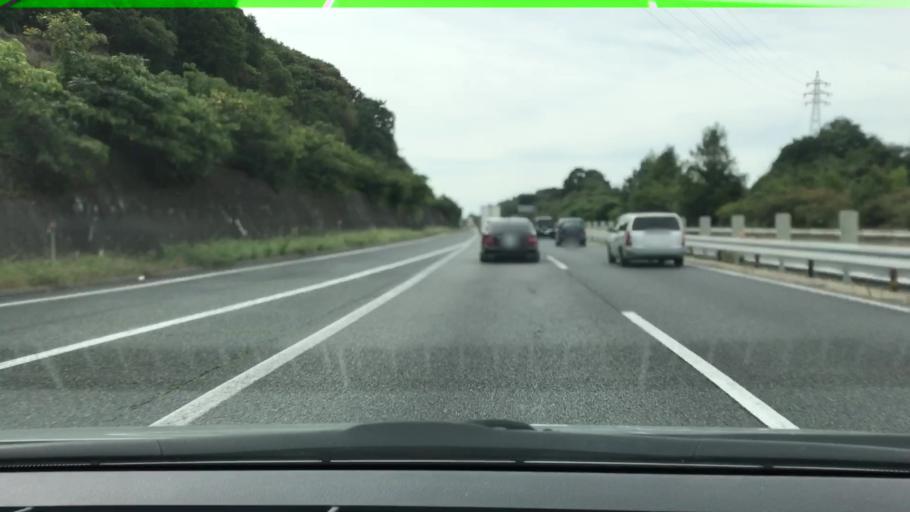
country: JP
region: Hyogo
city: Aioi
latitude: 34.8198
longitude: 134.4600
